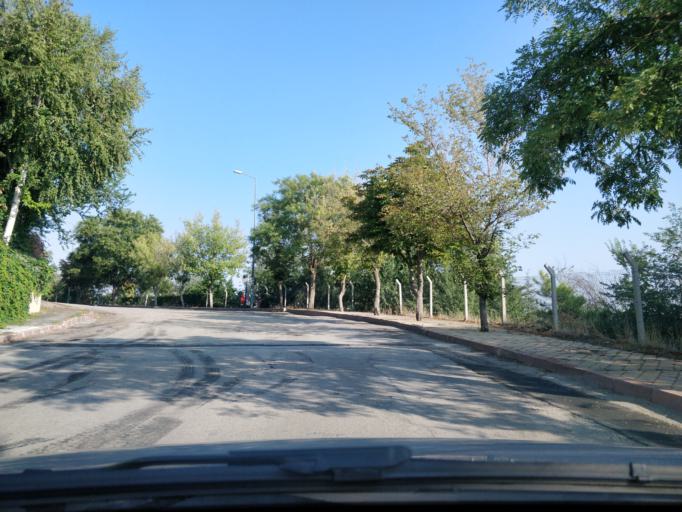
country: TR
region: Ankara
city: Batikent
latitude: 39.8962
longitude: 32.7257
